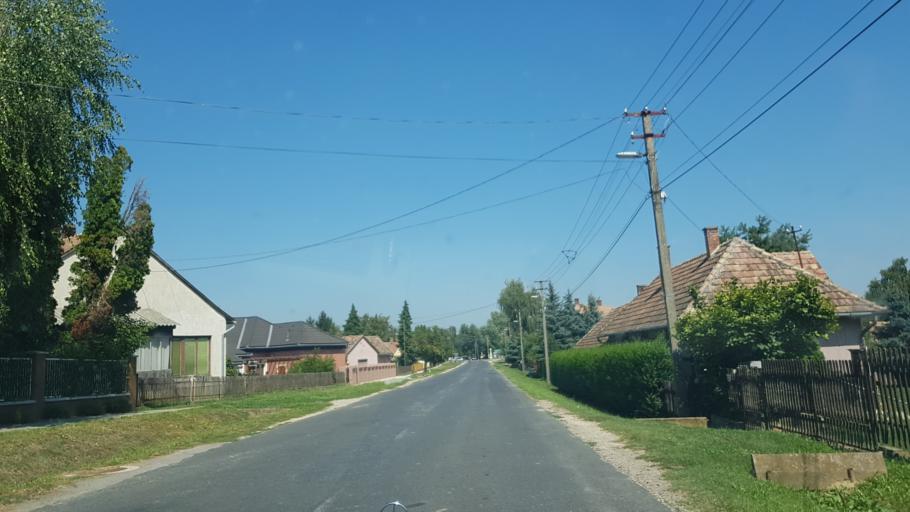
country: HU
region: Somogy
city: Segesd
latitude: 46.3407
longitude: 17.3452
